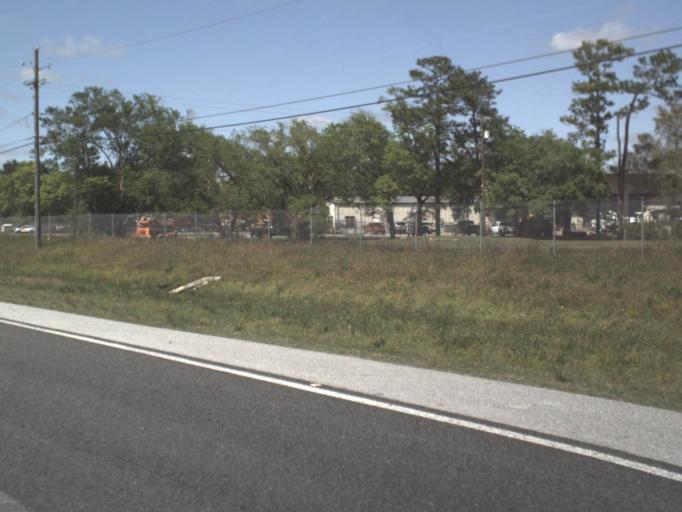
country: US
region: Florida
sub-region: Escambia County
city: Ensley
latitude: 30.5079
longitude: -87.2684
